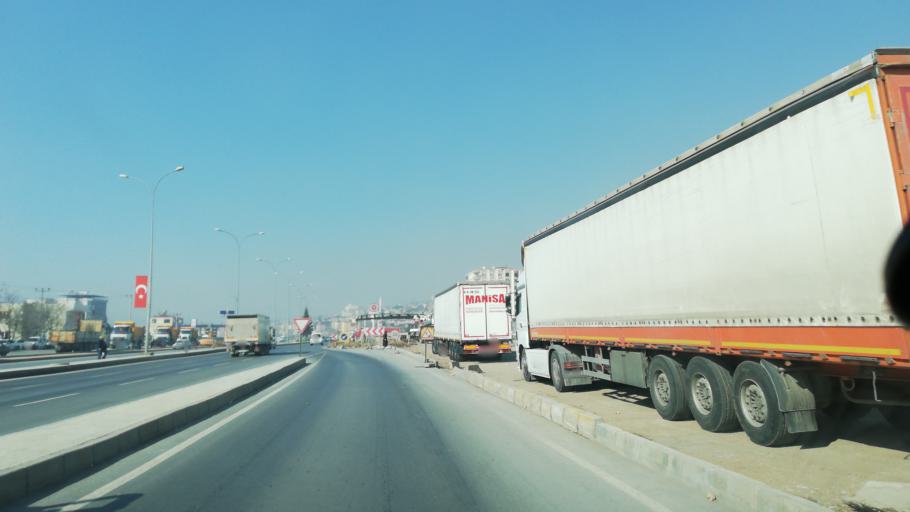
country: TR
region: Kahramanmaras
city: Kahramanmaras
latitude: 37.5693
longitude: 36.9214
